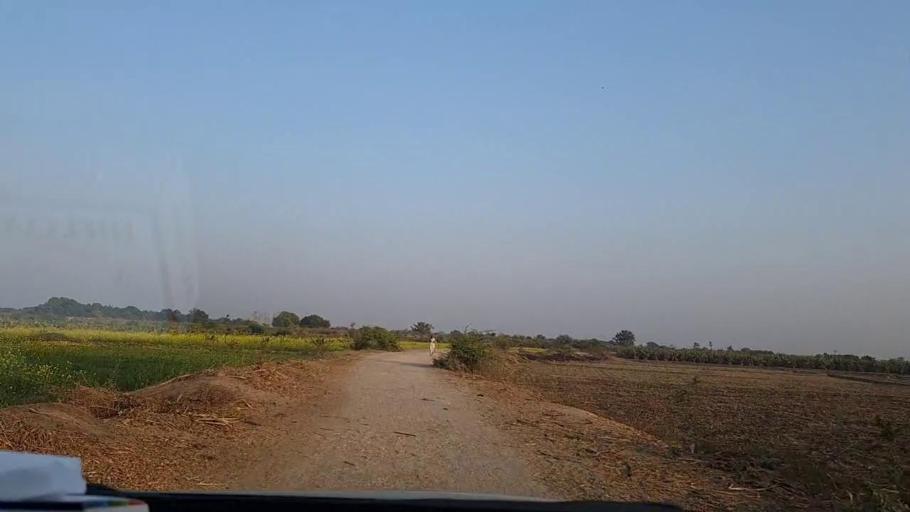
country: PK
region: Sindh
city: Tando Ghulam Ali
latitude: 25.1862
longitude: 68.9122
